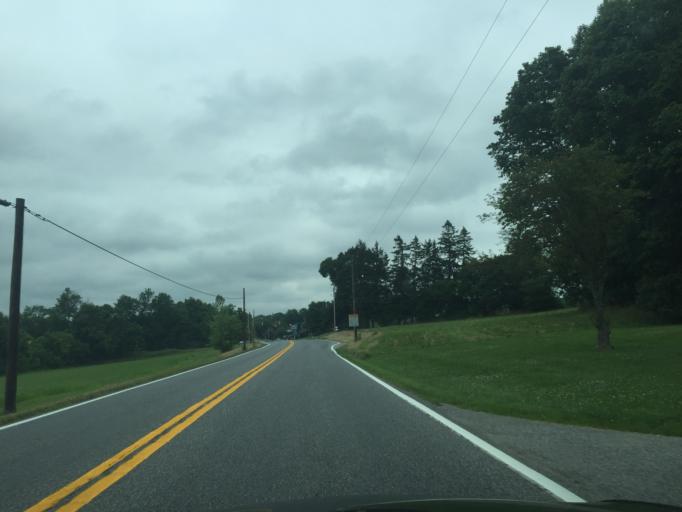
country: US
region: Maryland
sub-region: Harford County
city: Jarrettsville
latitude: 39.5526
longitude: -76.5264
